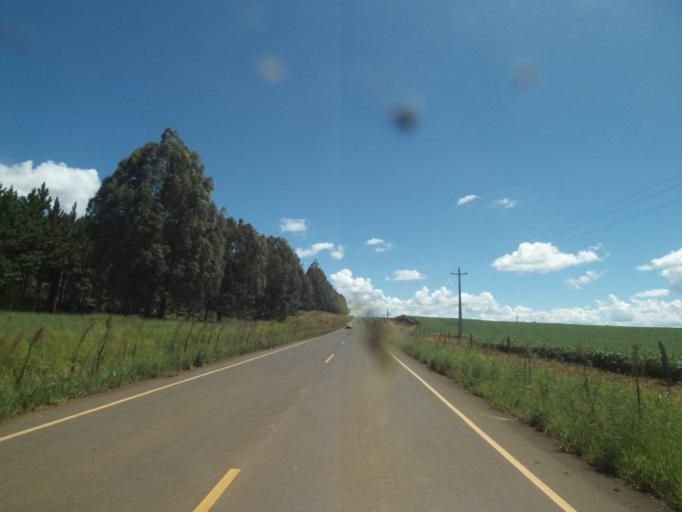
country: BR
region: Parana
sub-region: Pinhao
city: Pinhao
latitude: -25.8290
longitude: -52.0187
